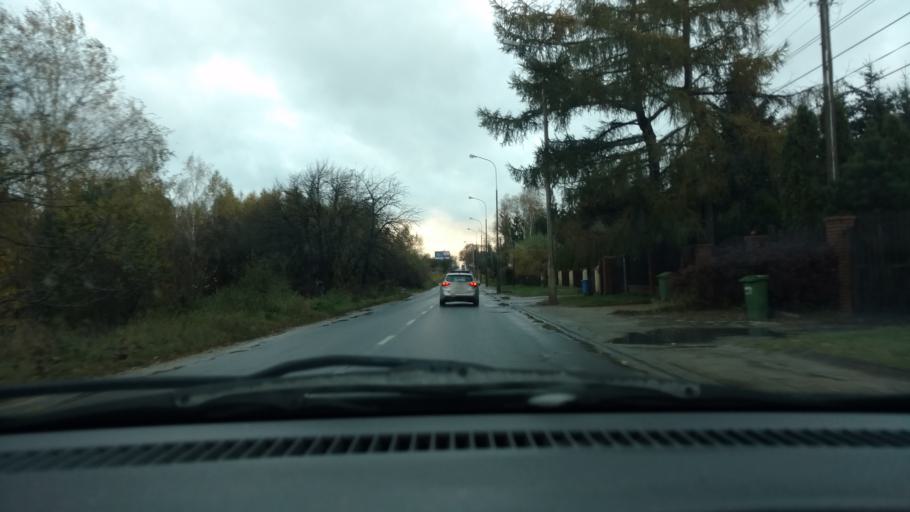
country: PL
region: Lodz Voivodeship
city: Lodz
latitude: 51.7713
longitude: 19.5576
